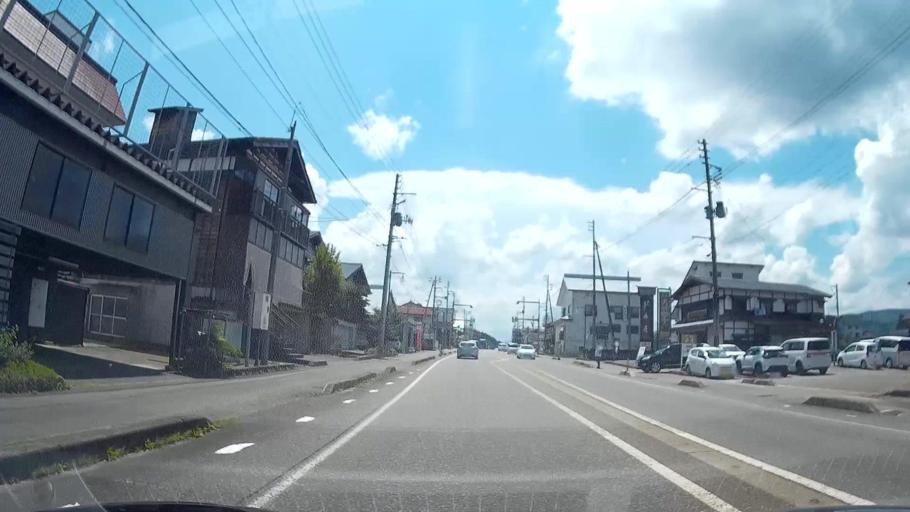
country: JP
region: Niigata
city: Tokamachi
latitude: 37.0988
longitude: 138.7336
